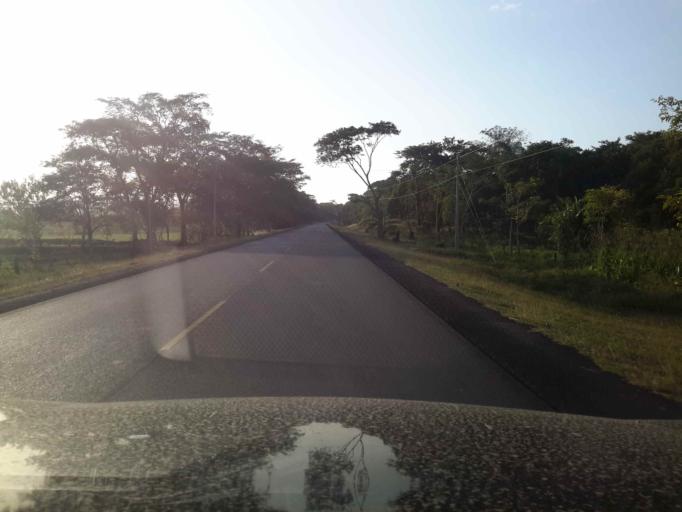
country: NI
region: Rio San Juan
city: San Miguelito
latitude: 11.3955
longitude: -84.8121
